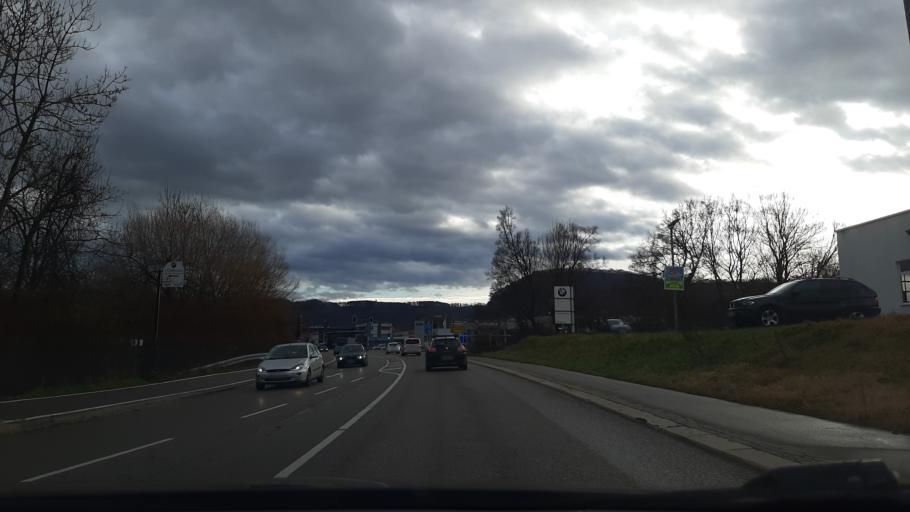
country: DE
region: Baden-Wuerttemberg
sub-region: Regierungsbezirk Stuttgart
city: Kuchen
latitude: 48.6316
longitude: 9.8067
